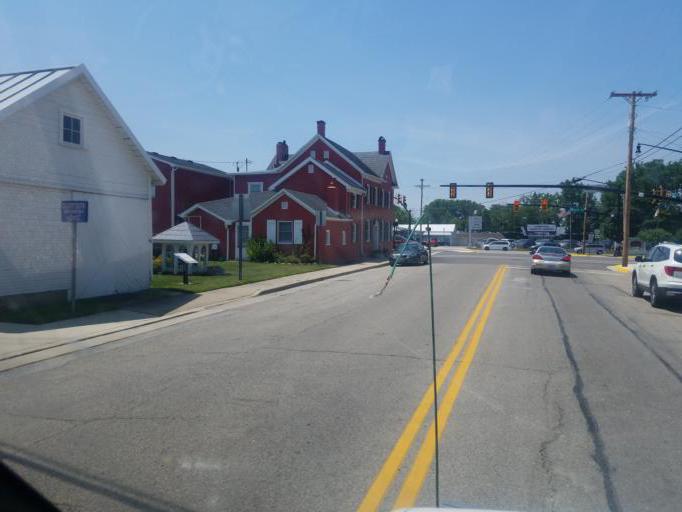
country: US
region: Ohio
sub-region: Shelby County
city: Fort Loramie
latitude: 40.3513
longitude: -84.3737
